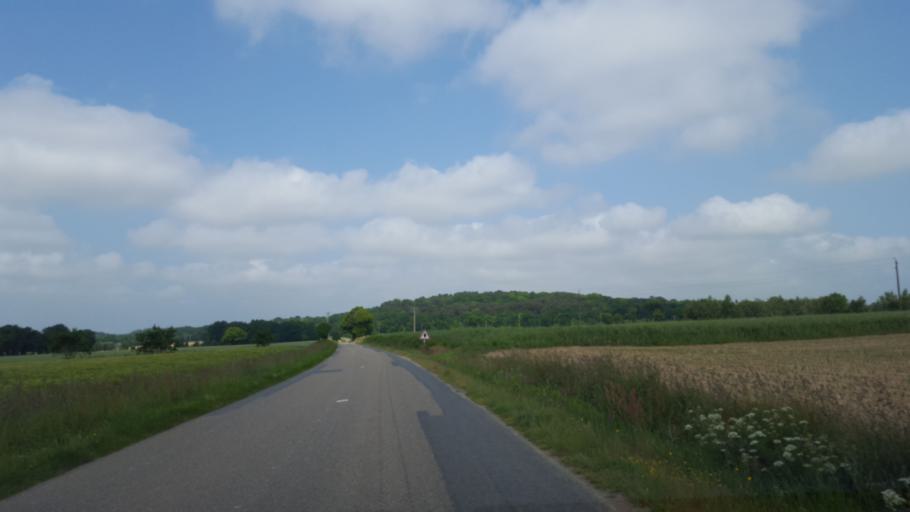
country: FR
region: Brittany
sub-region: Departement d'Ille-et-Vilaine
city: Guignen
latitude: 47.9244
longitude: -1.8872
